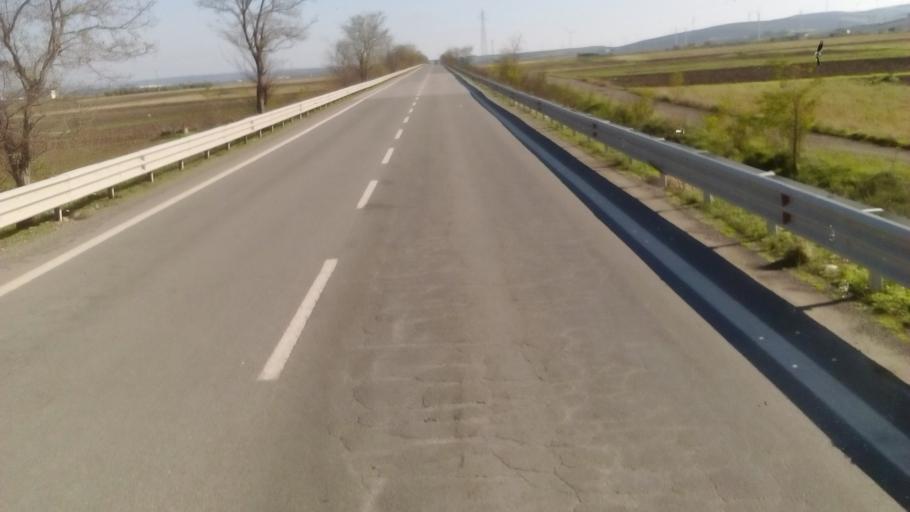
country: IT
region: Basilicate
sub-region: Provincia di Potenza
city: Zona 179
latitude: 41.0799
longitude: 15.6303
